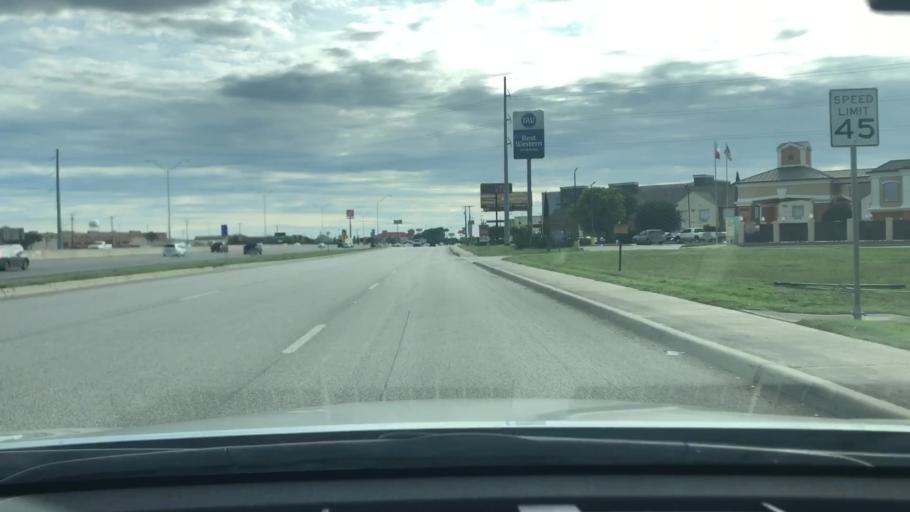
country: US
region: Texas
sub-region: Comal County
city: New Braunfels
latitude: 29.7089
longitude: -98.0905
